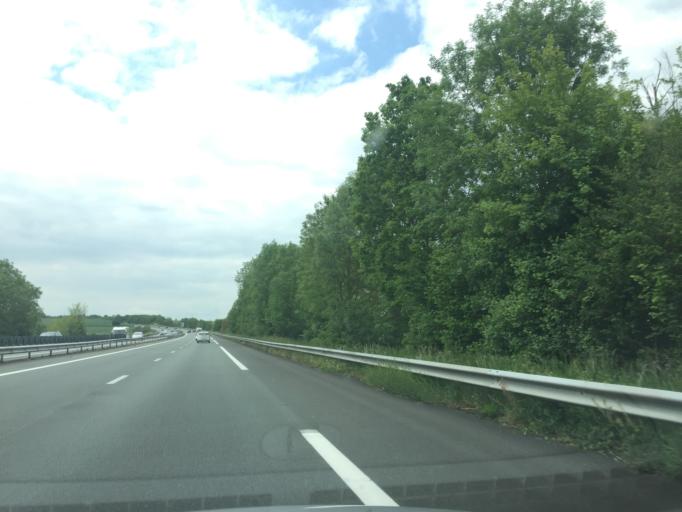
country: FR
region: Poitou-Charentes
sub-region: Departement des Deux-Sevres
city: Nanteuil
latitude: 46.3943
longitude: -0.1827
